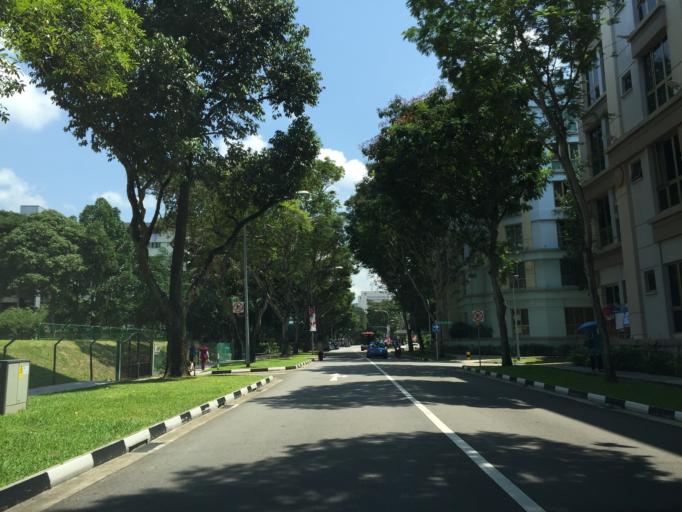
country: SG
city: Singapore
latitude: 1.3149
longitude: 103.8520
